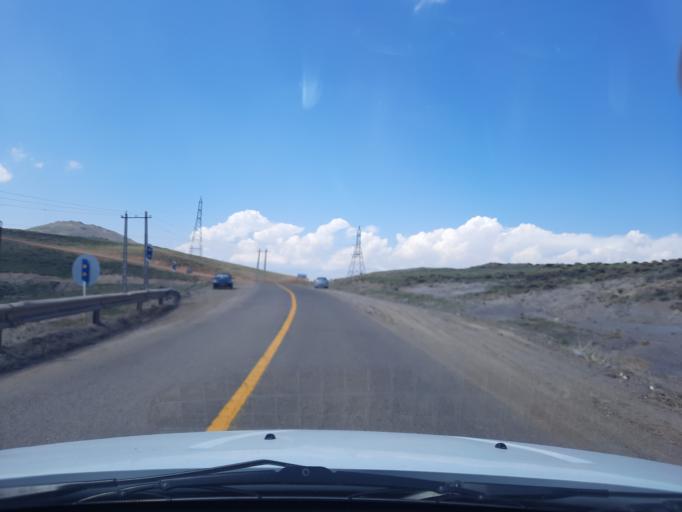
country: IR
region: Qazvin
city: Qazvin
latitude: 36.3920
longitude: 50.2077
